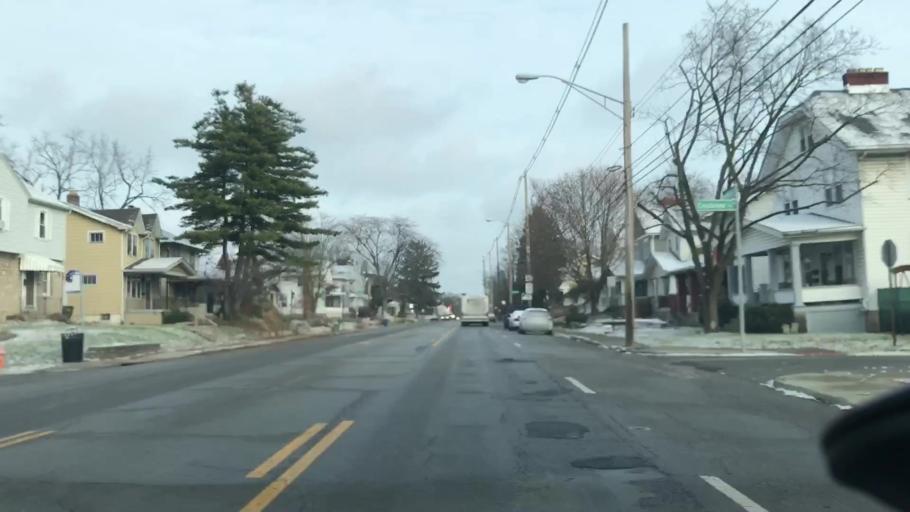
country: US
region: Ohio
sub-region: Franklin County
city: Grandview Heights
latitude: 40.0219
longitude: -83.0018
